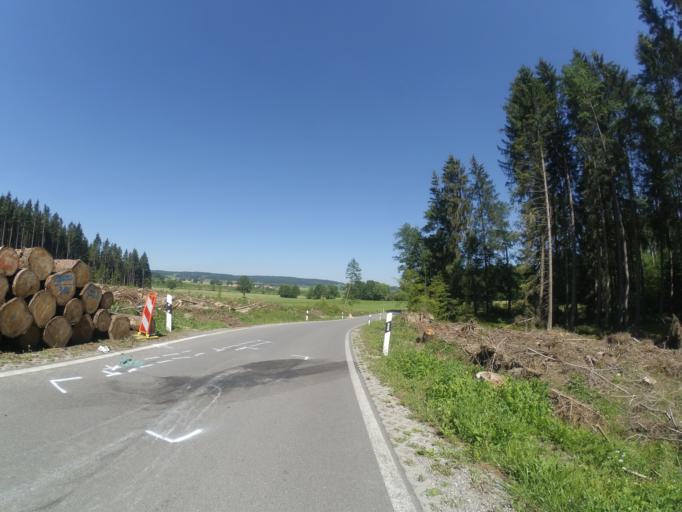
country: DE
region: Baden-Wuerttemberg
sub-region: Tuebingen Region
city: Bad Wurzach
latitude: 47.8592
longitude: 9.9364
